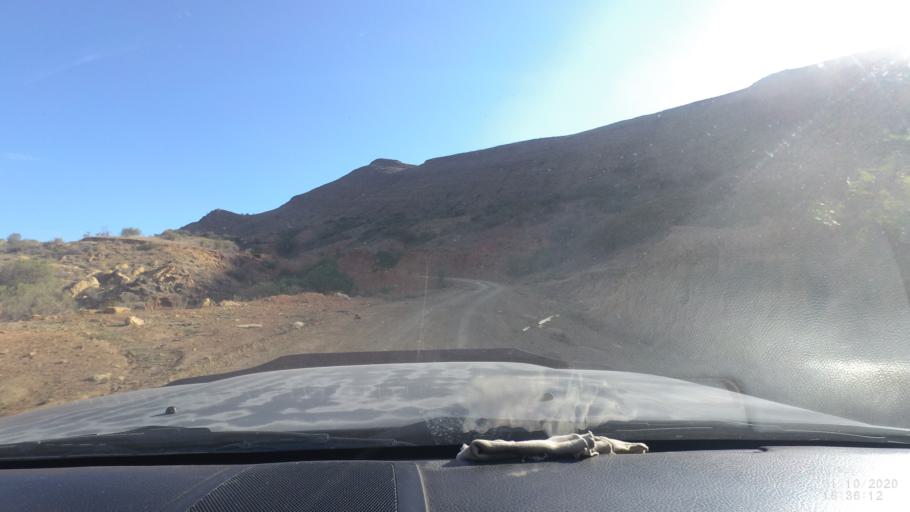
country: BO
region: Chuquisaca
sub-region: Provincia Zudanez
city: Mojocoya
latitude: -18.4581
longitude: -64.5827
